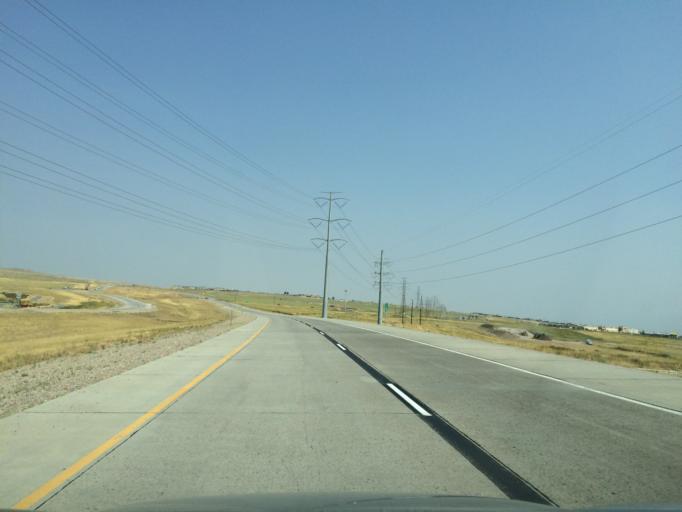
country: US
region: Utah
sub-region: Salt Lake County
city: Oquirrh
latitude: 40.6027
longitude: -112.0295
